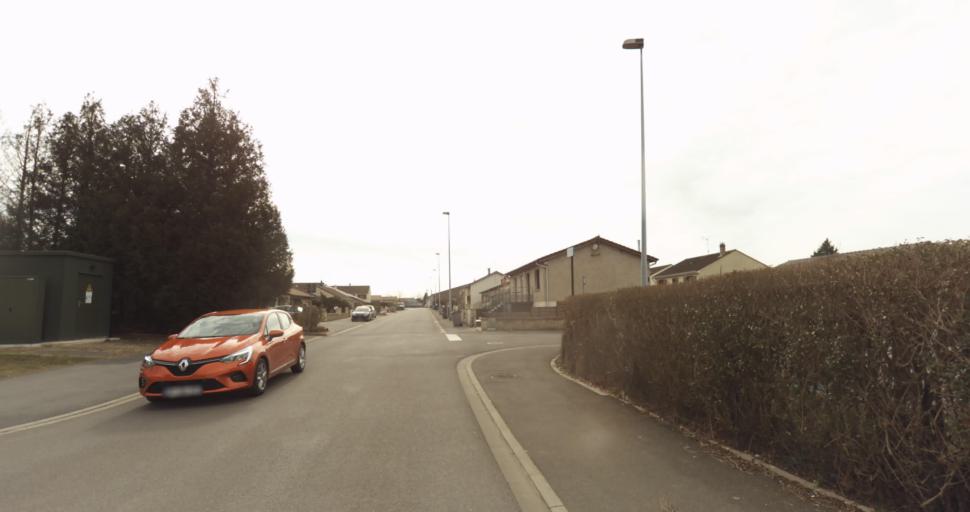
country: FR
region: Lorraine
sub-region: Departement de Meurthe-et-Moselle
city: Jarny
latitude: 49.1581
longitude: 5.8706
